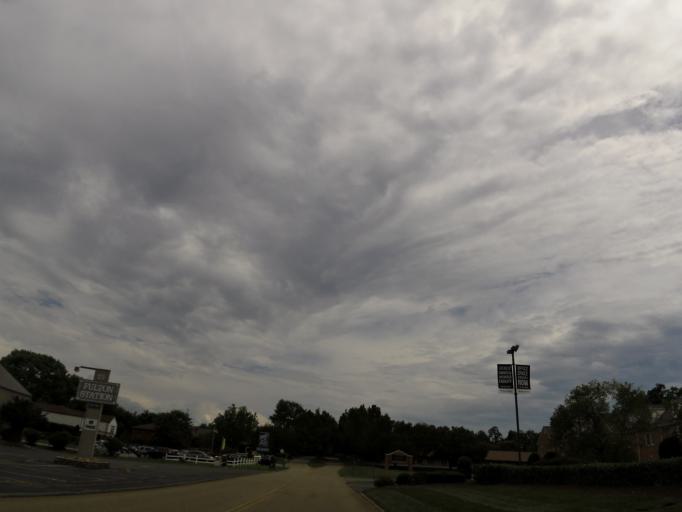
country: US
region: Tennessee
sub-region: Knox County
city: Farragut
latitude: 35.9056
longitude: -84.1219
